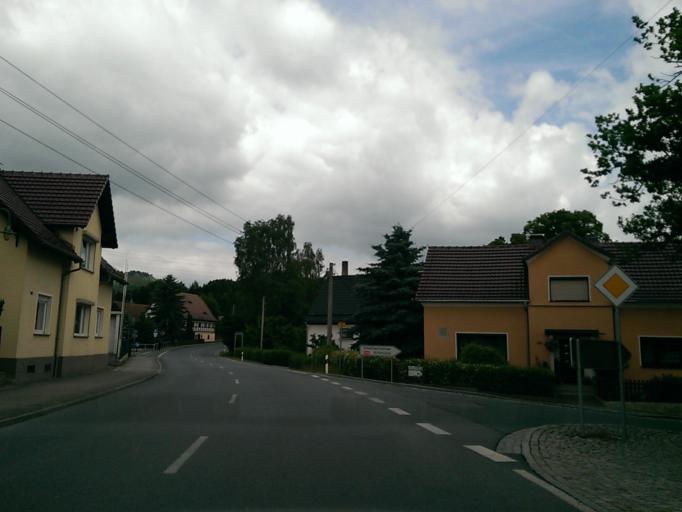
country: DE
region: Saxony
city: Hainewalde
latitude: 50.9593
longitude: 14.7180
